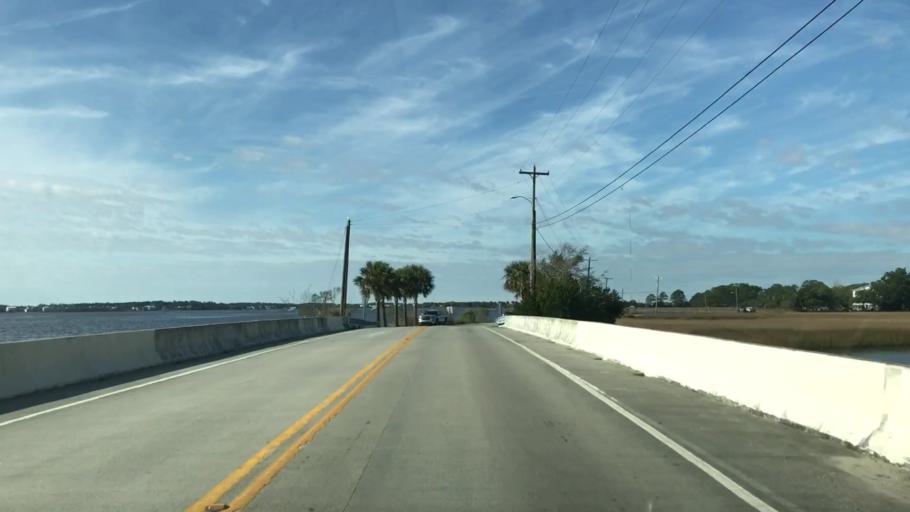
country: US
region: South Carolina
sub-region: Charleston County
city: Charleston
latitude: 32.7719
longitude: -80.0069
